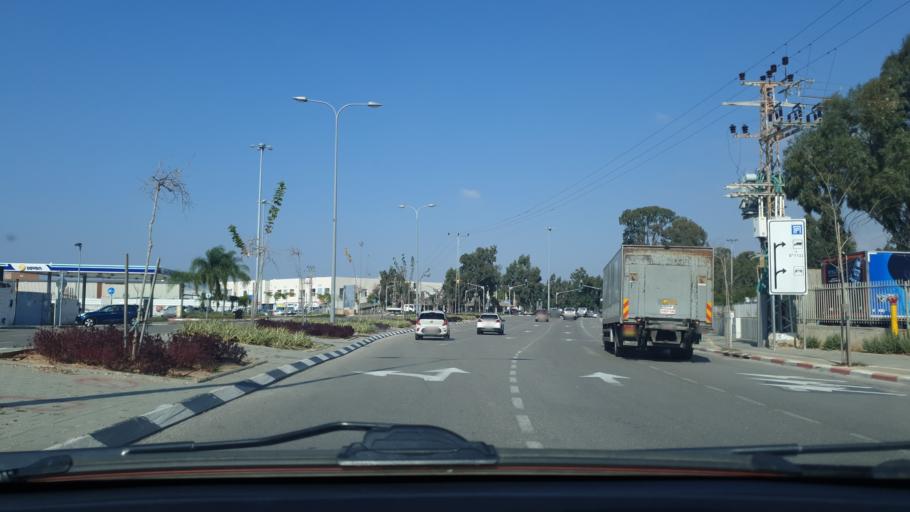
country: IL
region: Tel Aviv
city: Azor
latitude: 32.0131
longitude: 34.8084
